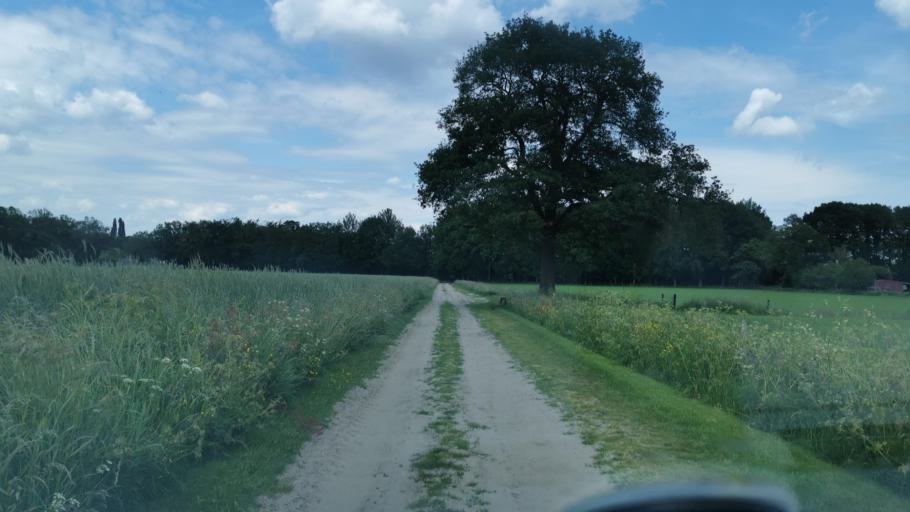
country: NL
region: Overijssel
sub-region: Gemeente Enschede
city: Enschede
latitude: 52.2561
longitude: 6.9203
